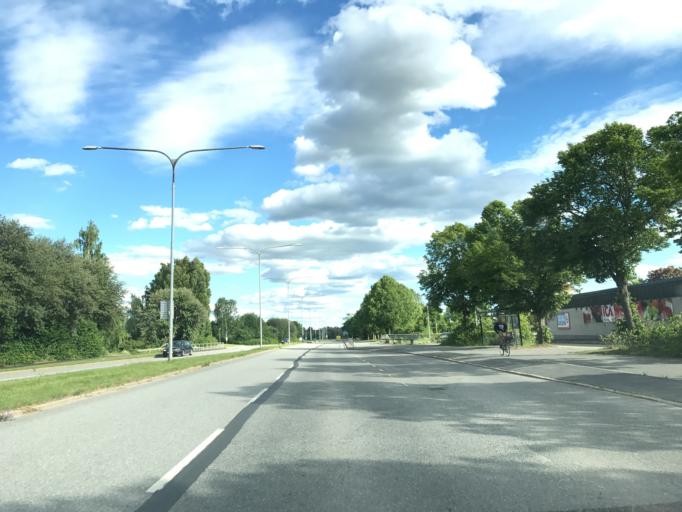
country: SE
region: OErebro
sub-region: Orebro Kommun
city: Orebro
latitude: 59.2937
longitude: 15.1691
